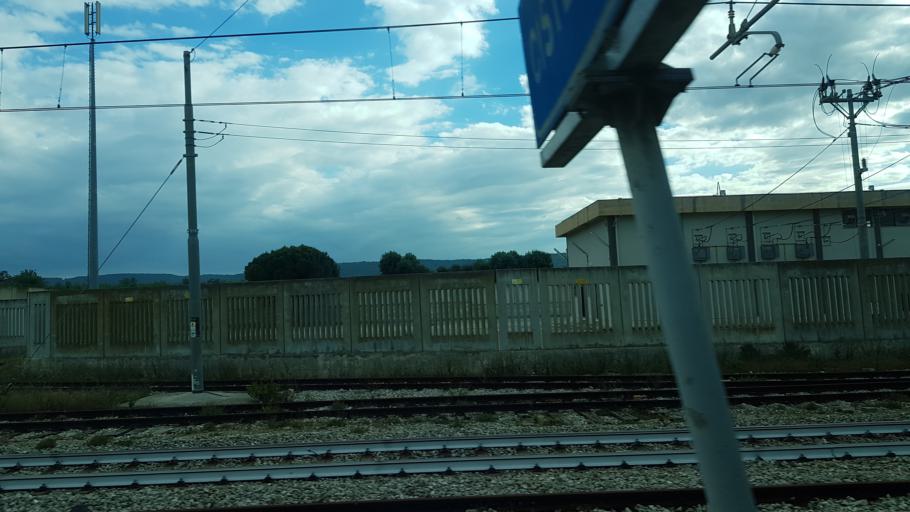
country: IT
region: Apulia
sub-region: Provincia di Brindisi
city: Pezze di Greco
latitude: 40.8174
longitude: 17.4552
